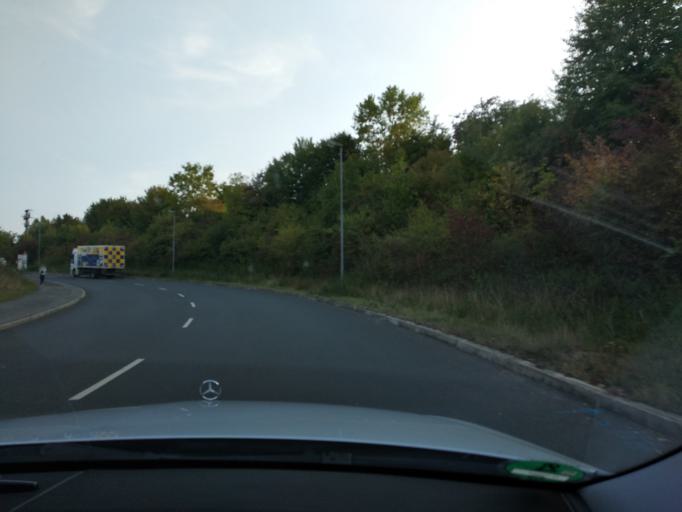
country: DE
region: Baden-Wuerttemberg
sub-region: Regierungsbezirk Stuttgart
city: Tauberbischofsheim
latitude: 49.6381
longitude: 9.6500
